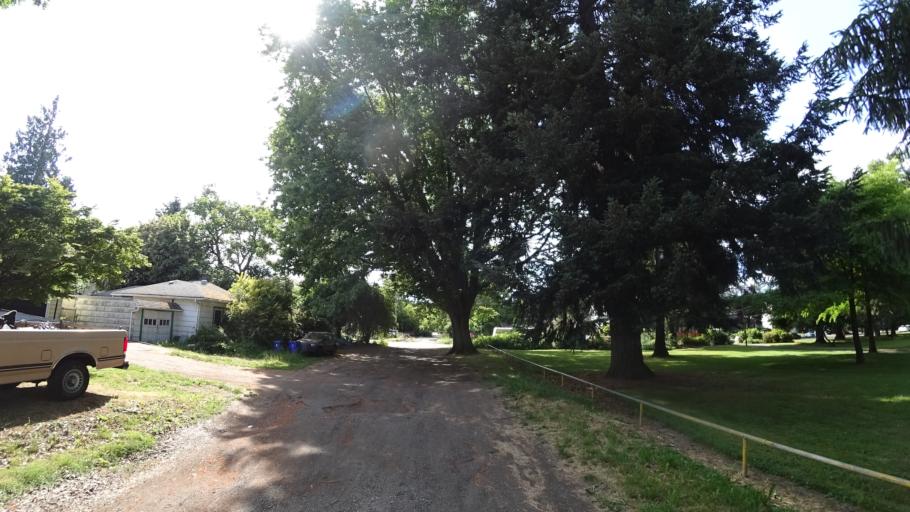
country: US
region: Oregon
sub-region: Washington County
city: West Haven
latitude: 45.5930
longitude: -122.7393
